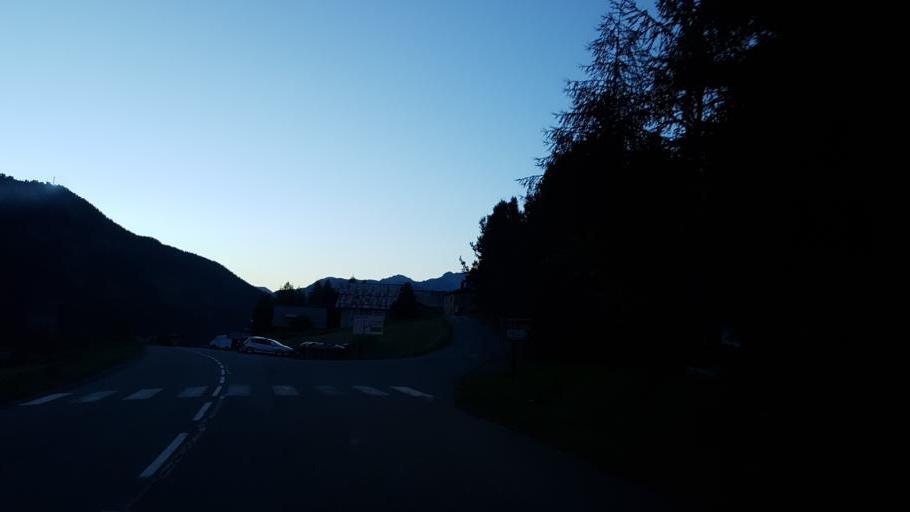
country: FR
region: Provence-Alpes-Cote d'Azur
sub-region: Departement des Hautes-Alpes
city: Guillestre
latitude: 44.7281
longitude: 6.8448
